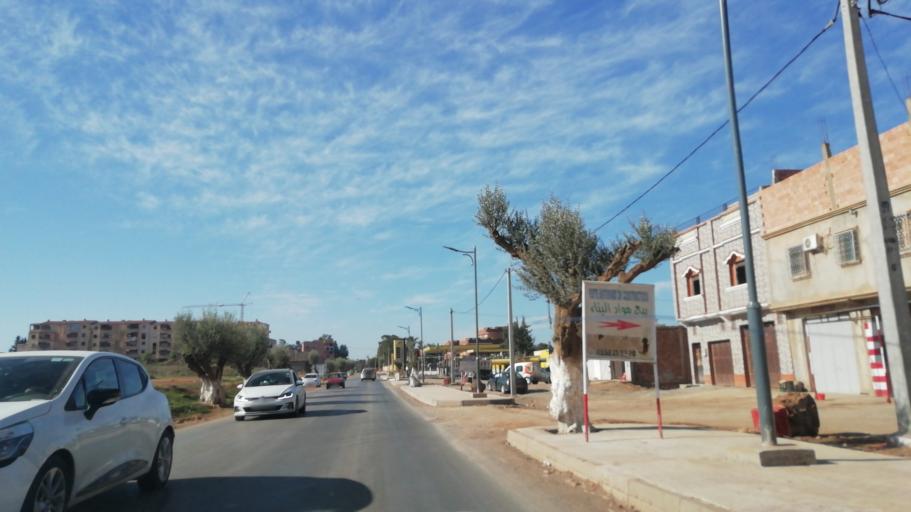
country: DZ
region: Tlemcen
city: Ouled Mimoun
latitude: 35.0276
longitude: -0.8814
